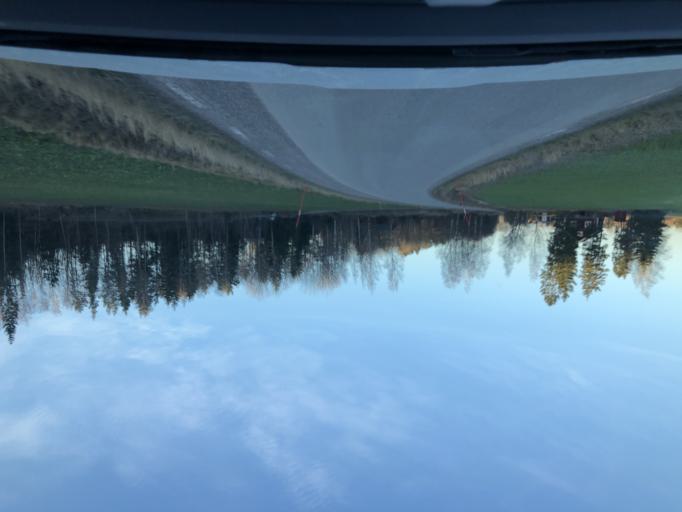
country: SE
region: Soedermanland
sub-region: Eskilstuna Kommun
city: Arla
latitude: 59.4168
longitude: 16.6776
